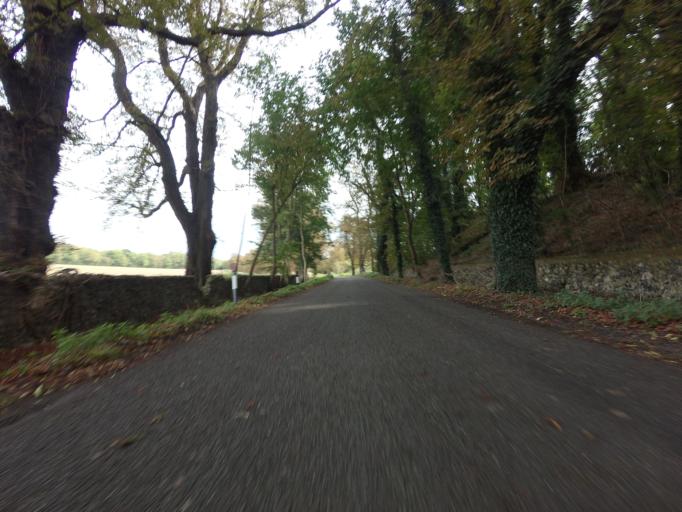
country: GB
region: England
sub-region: Essex
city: Saffron Walden
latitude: 52.0181
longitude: 0.2055
